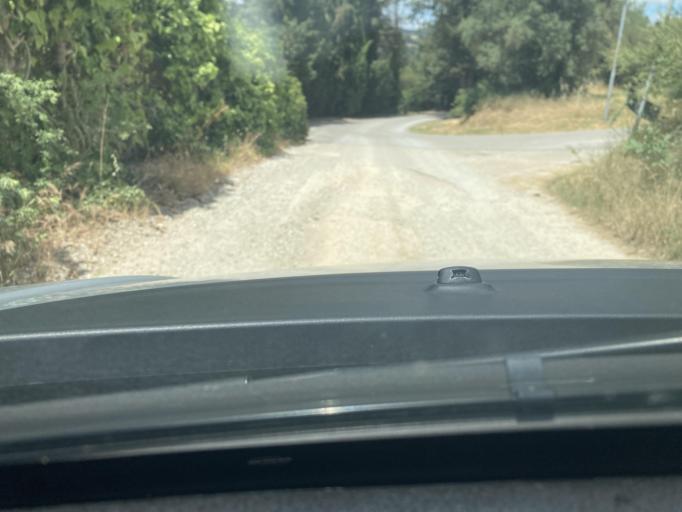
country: IT
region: Umbria
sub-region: Provincia di Perugia
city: Corciano
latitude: 43.1297
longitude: 12.2638
